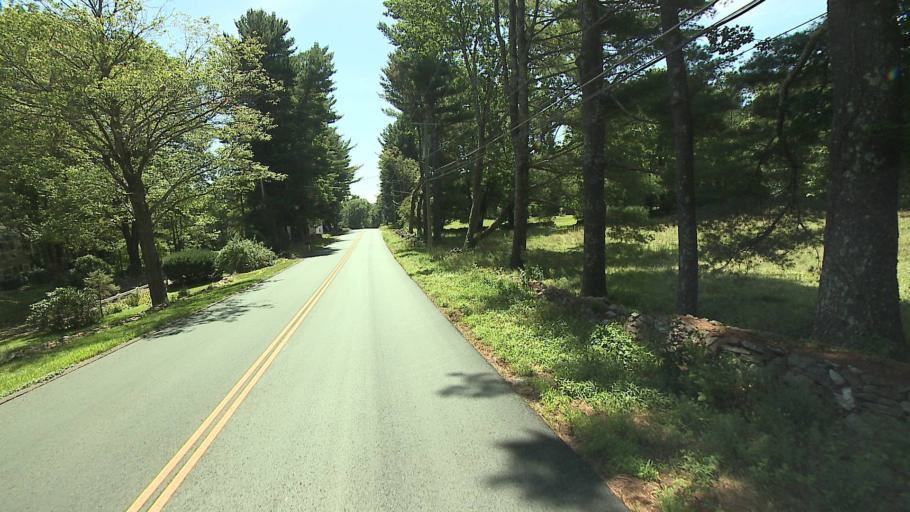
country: US
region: Connecticut
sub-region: Hartford County
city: West Simsbury
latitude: 41.9146
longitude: -72.9019
